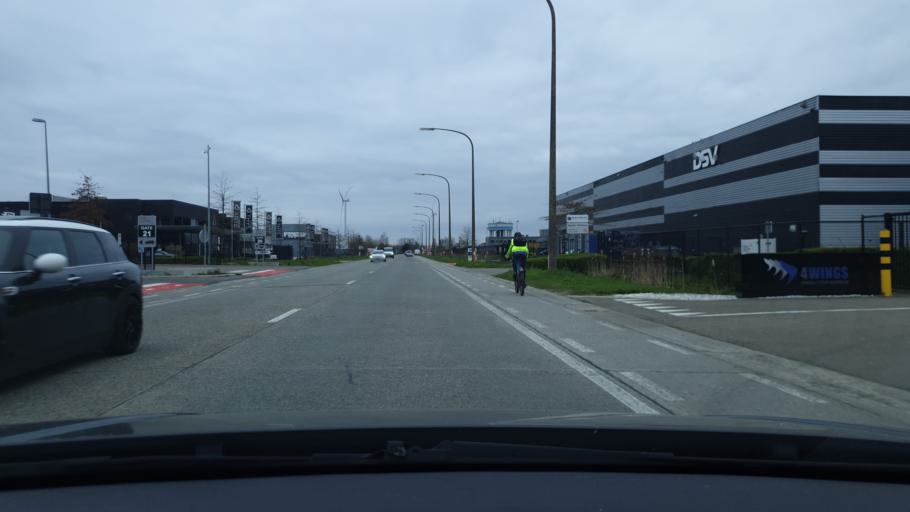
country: BE
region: Flanders
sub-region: Provincie Antwerpen
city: Westerlo
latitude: 51.1365
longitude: 4.9272
